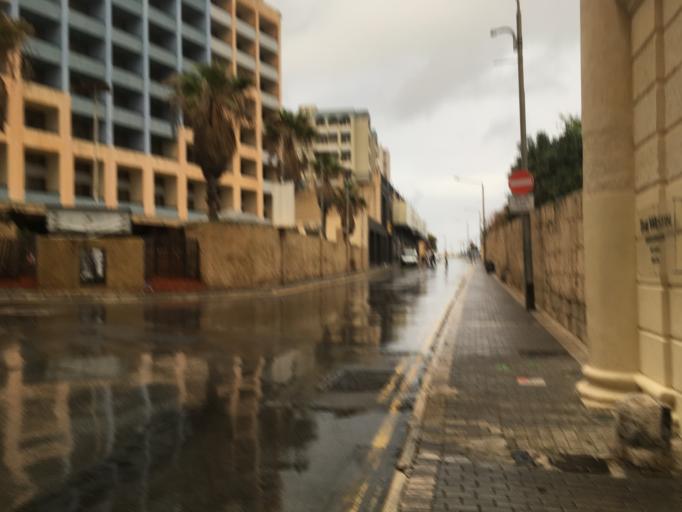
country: MT
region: Saint Julian
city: San Giljan
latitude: 35.9243
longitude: 14.4916
